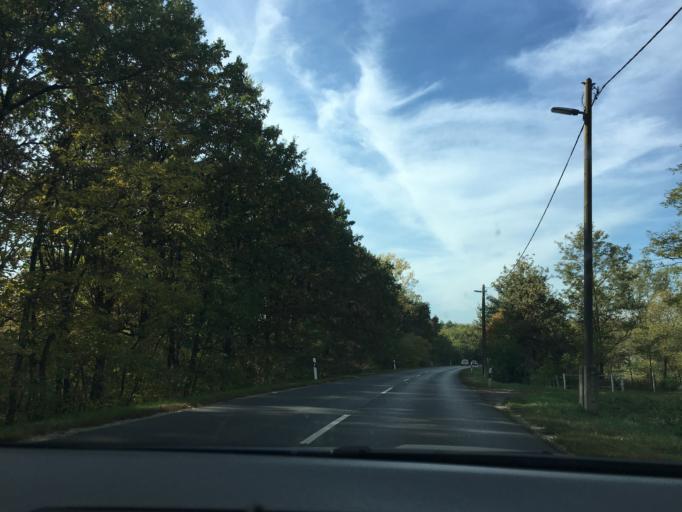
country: HU
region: Hajdu-Bihar
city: Vamospercs
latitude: 47.5236
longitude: 21.8740
